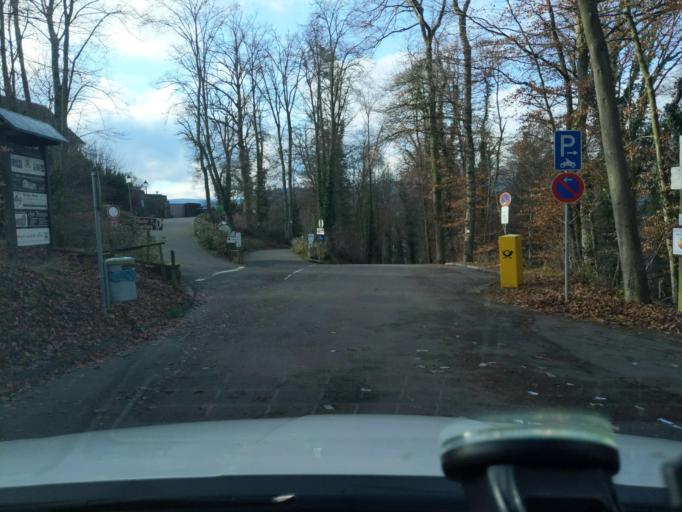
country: DE
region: Bavaria
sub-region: Regierungsbezirk Unterfranken
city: Grossheubach
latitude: 49.7248
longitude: 9.2334
